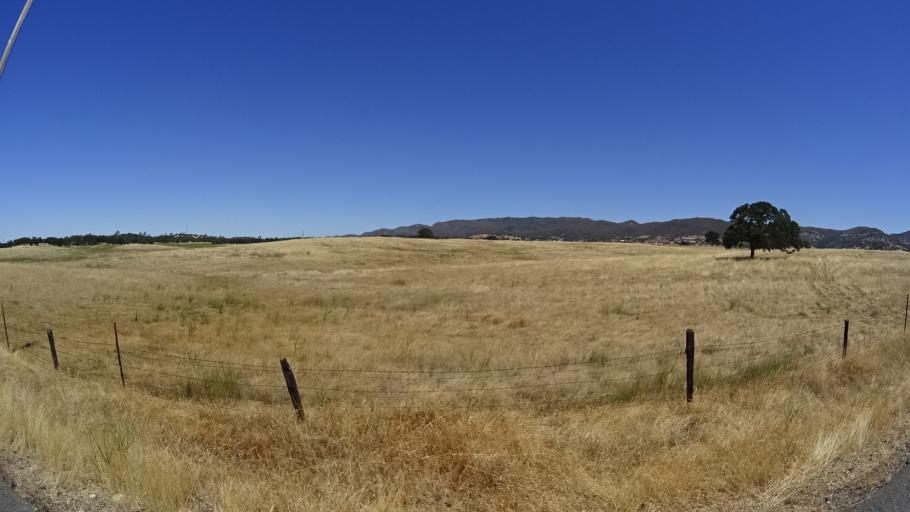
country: US
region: California
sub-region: Calaveras County
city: Copperopolis
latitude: 38.0537
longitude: -120.7428
